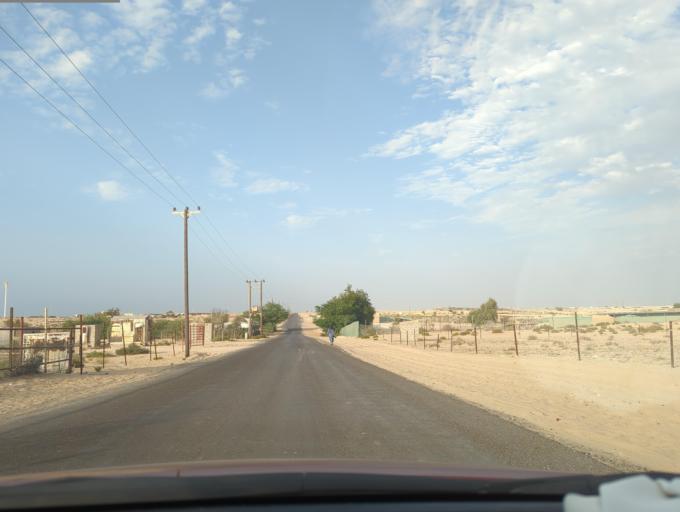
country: AE
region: Dubai
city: Dubai
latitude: 24.7157
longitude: 54.8690
